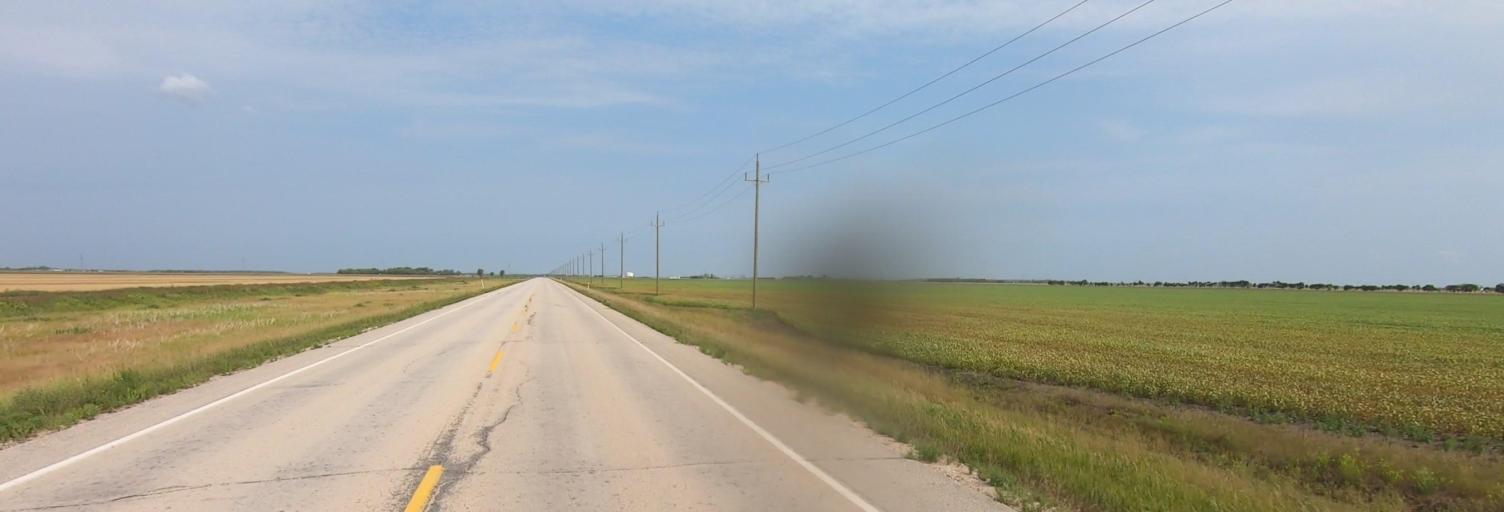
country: CA
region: Manitoba
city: Winnipeg
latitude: 49.7169
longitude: -97.2551
